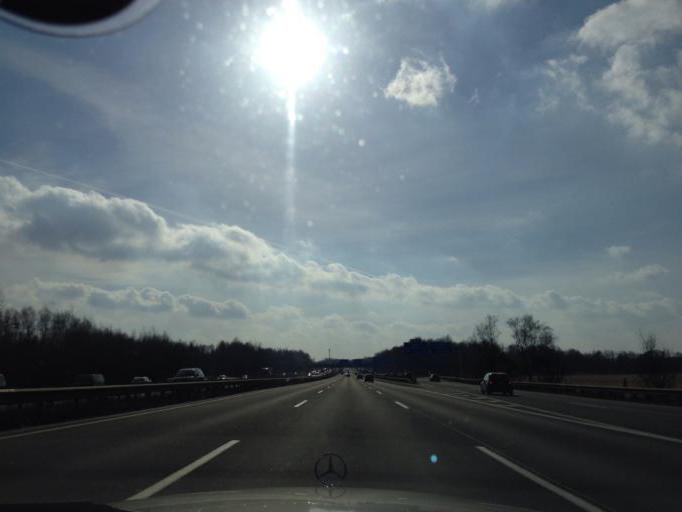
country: DE
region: Lower Saxony
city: Seevetal
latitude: 53.3963
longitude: 10.0248
